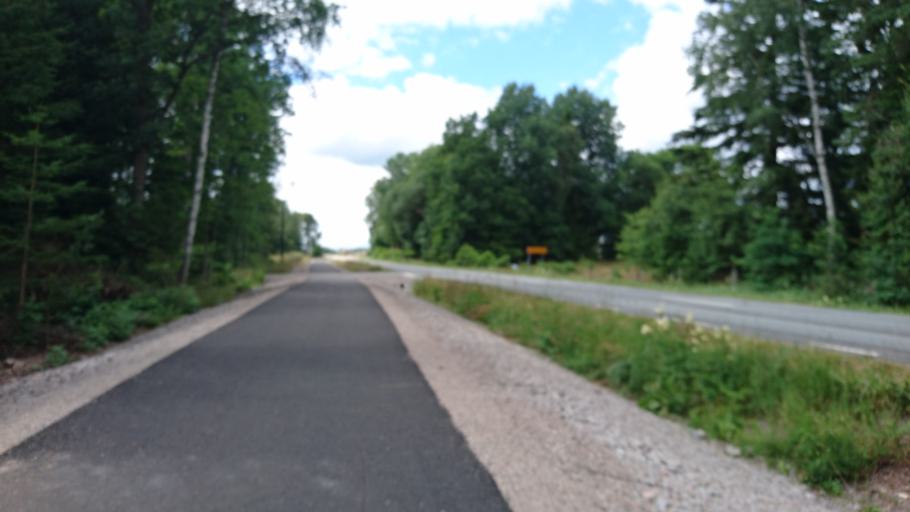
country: SE
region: Kronoberg
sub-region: Alvesta Kommun
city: Moheda
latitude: 56.9889
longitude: 14.6010
